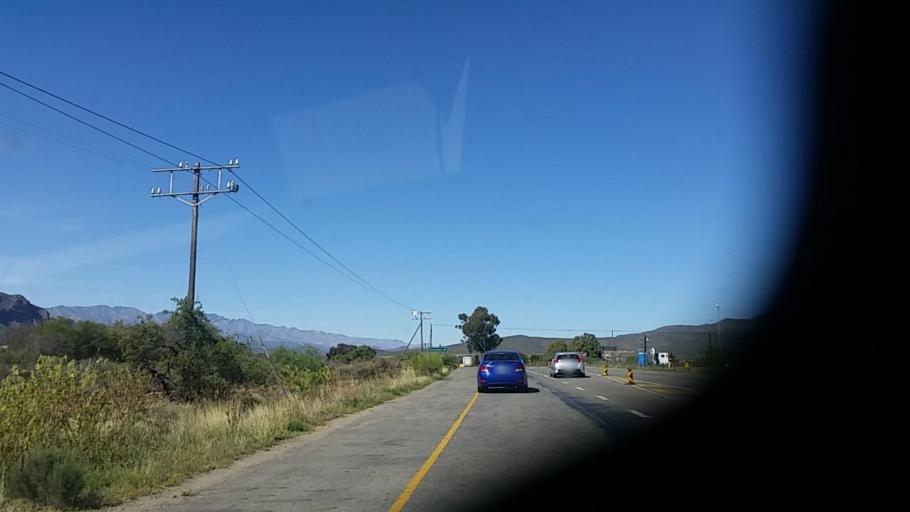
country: ZA
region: Western Cape
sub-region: Eden District Municipality
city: Oudtshoorn
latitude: -33.5617
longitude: 22.4141
